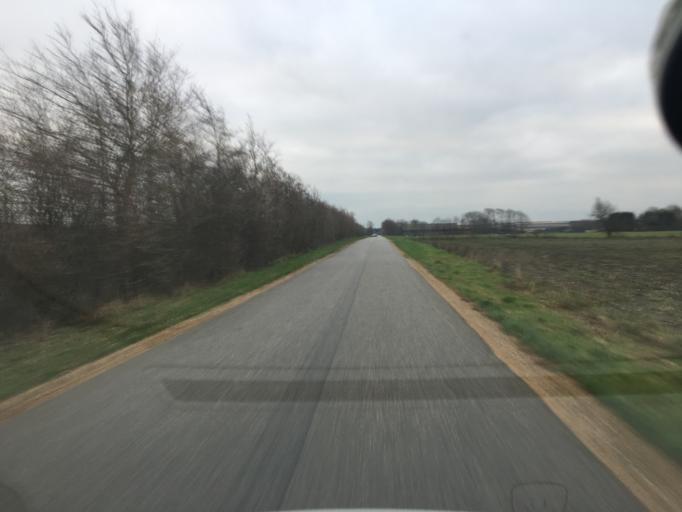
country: DK
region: South Denmark
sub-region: Tonder Kommune
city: Logumkloster
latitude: 55.0336
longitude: 9.0302
